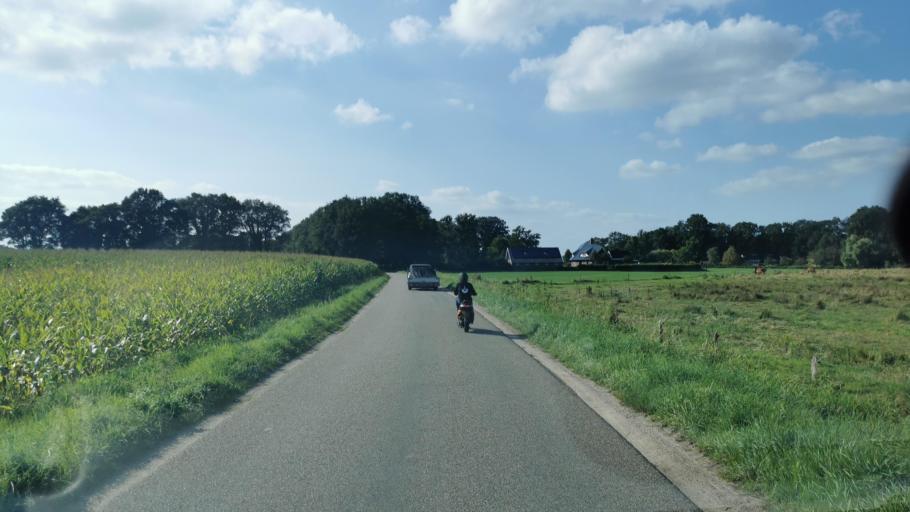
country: NL
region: Overijssel
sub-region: Gemeente Borne
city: Borne
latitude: 52.3354
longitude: 6.8058
